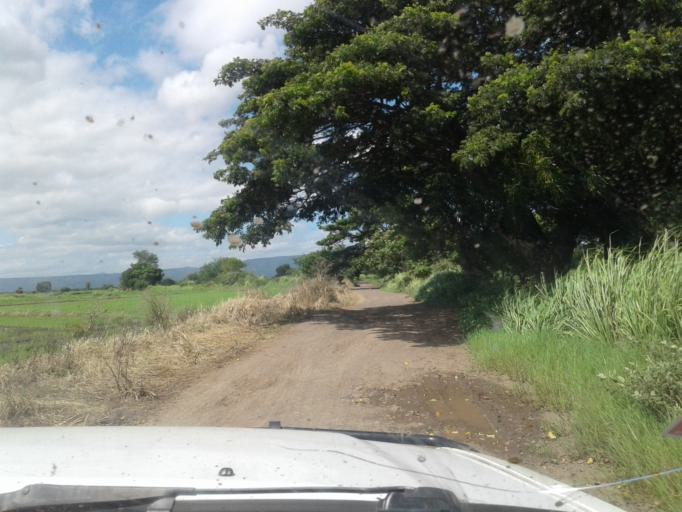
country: NI
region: Matagalpa
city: Ciudad Dario
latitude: 12.8450
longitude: -86.1424
